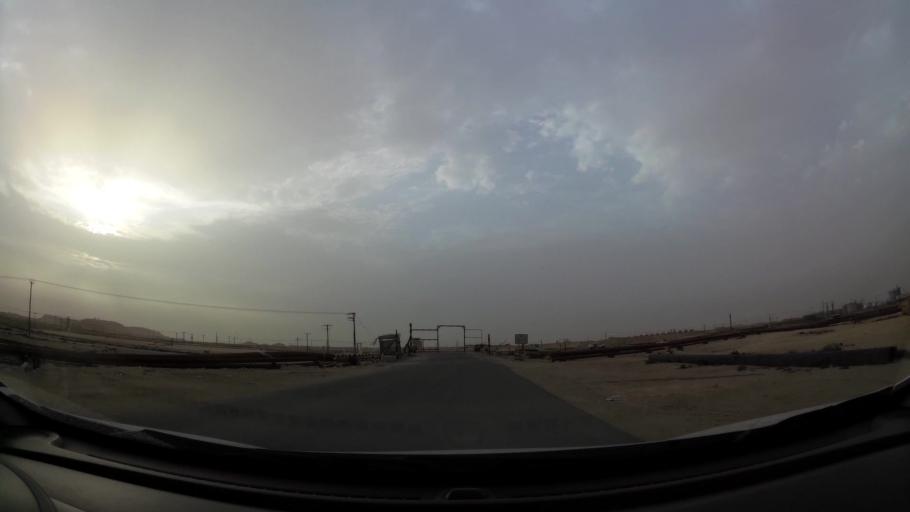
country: BH
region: Central Governorate
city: Dar Kulayb
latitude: 26.0413
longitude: 50.5749
